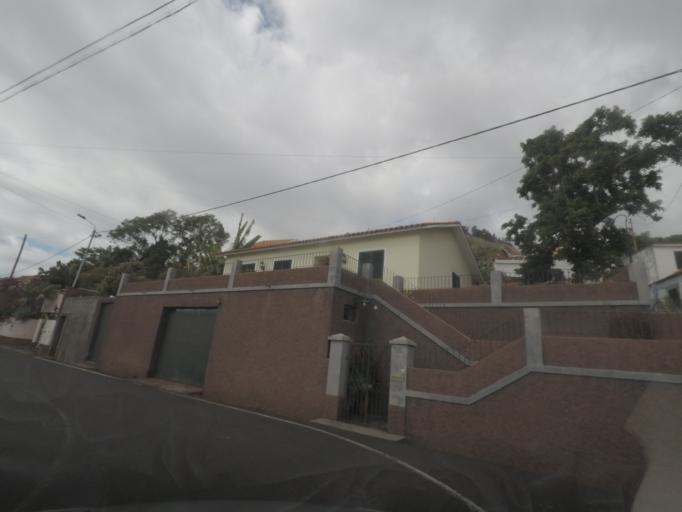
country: PT
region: Madeira
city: Camara de Lobos
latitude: 32.6466
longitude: -16.9435
